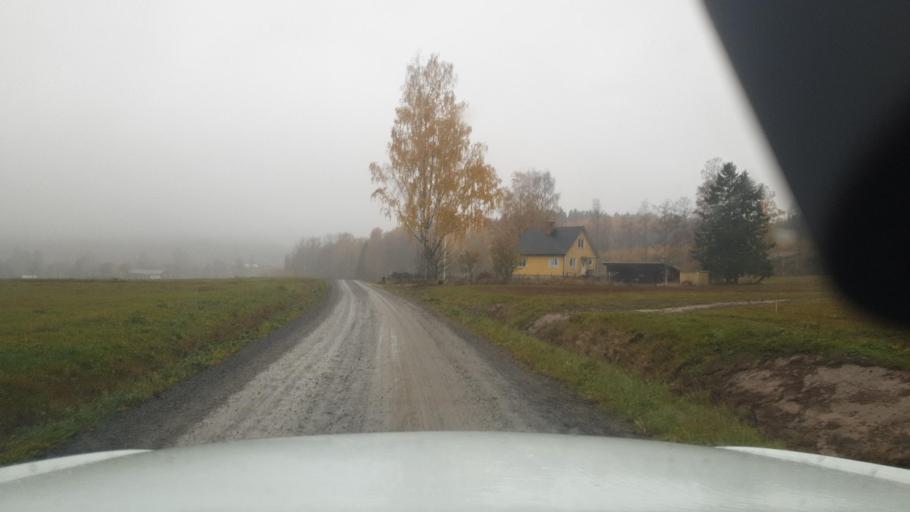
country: SE
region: Vaermland
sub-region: Sunne Kommun
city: Sunne
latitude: 59.8572
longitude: 12.9426
